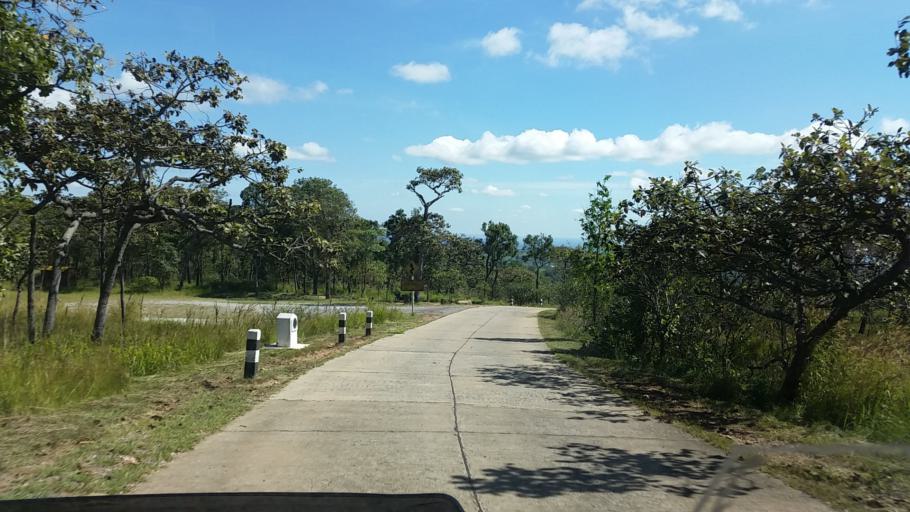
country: TH
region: Chaiyaphum
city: Sap Yai
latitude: 15.6421
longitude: 101.3877
